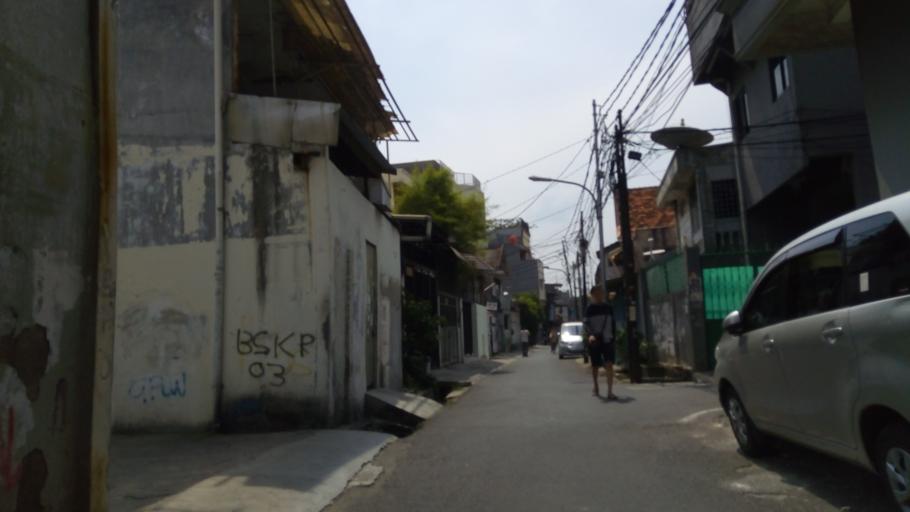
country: ID
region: Jakarta Raya
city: Jakarta
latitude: -6.1554
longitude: 106.8324
